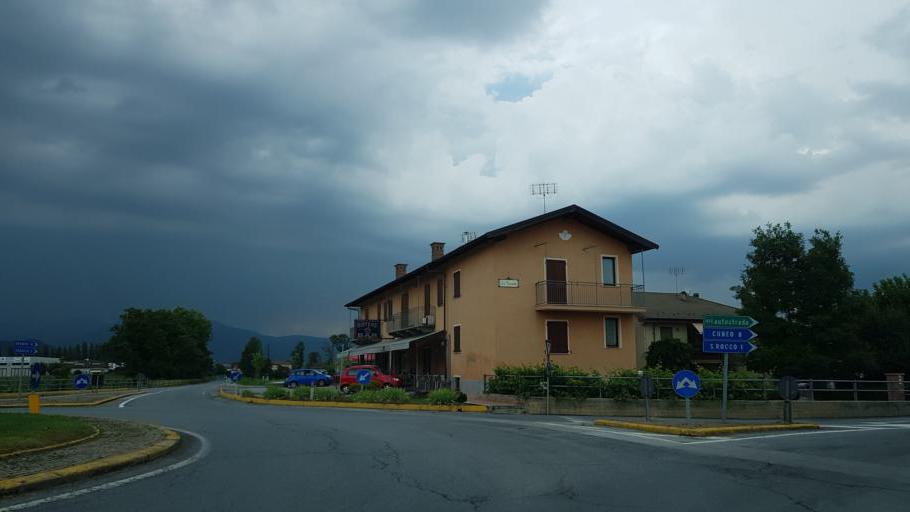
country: IT
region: Piedmont
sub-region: Provincia di Cuneo
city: San Rocco
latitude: 44.3909
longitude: 7.4586
